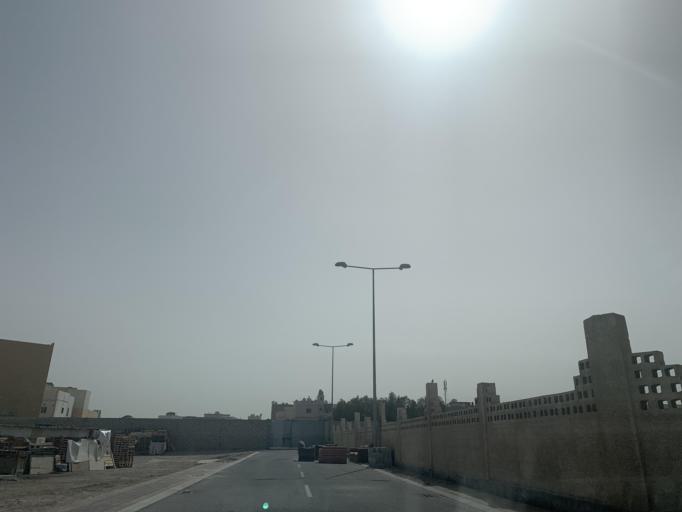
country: BH
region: Northern
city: Sitrah
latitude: 26.1697
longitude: 50.6248
